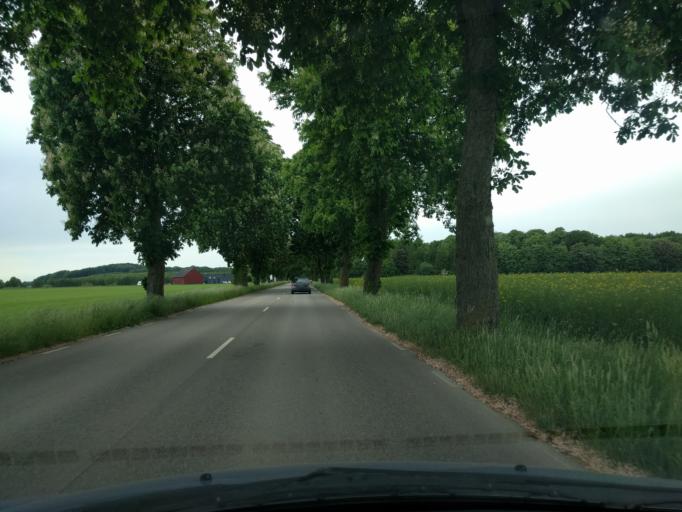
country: SE
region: Skane
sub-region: Malmo
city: Oxie
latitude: 55.5277
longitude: 13.1550
